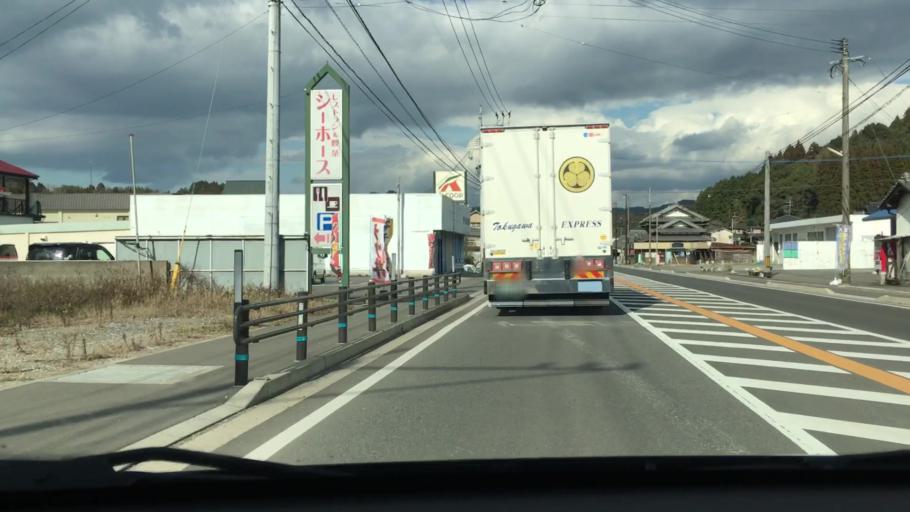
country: JP
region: Oita
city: Usuki
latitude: 33.0366
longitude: 131.6894
